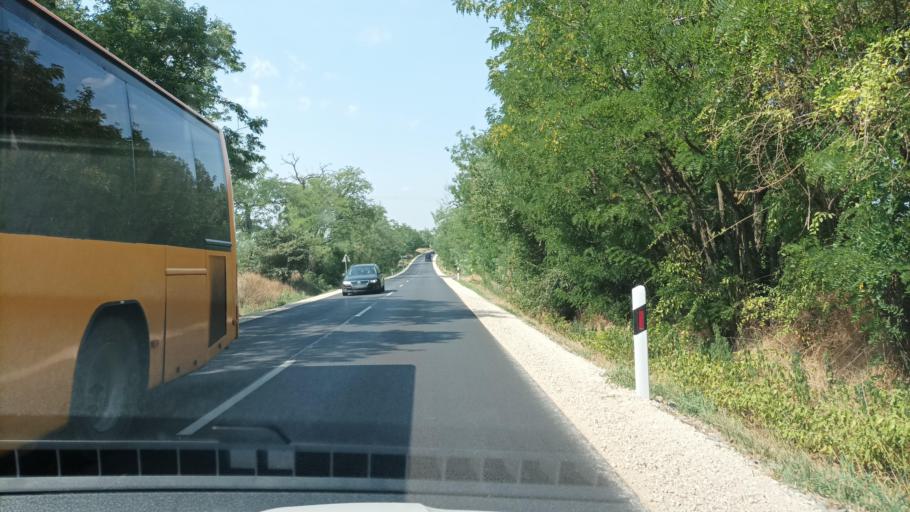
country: HU
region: Pest
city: Gomba
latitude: 47.3633
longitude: 19.4955
